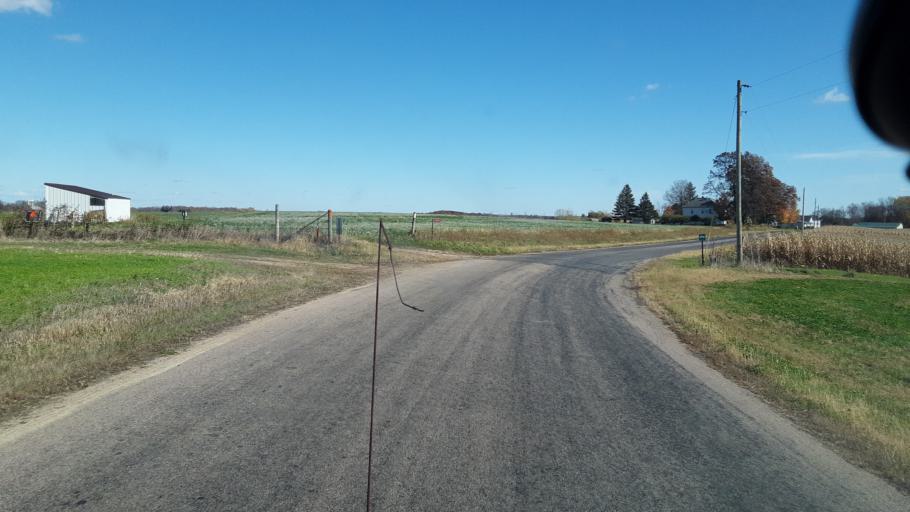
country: US
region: Wisconsin
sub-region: Vernon County
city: Hillsboro
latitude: 43.6928
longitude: -90.4332
